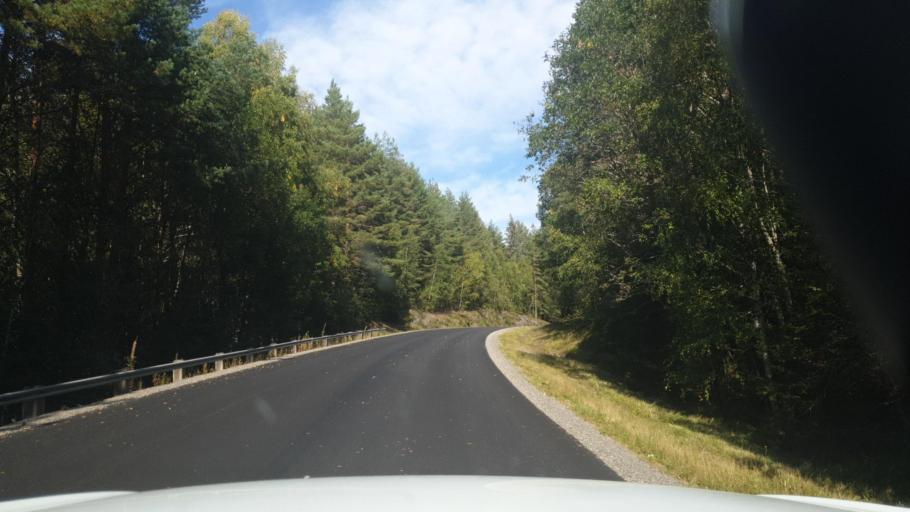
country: SE
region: Vaermland
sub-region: Arvika Kommun
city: Arvika
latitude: 59.9148
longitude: 12.6456
